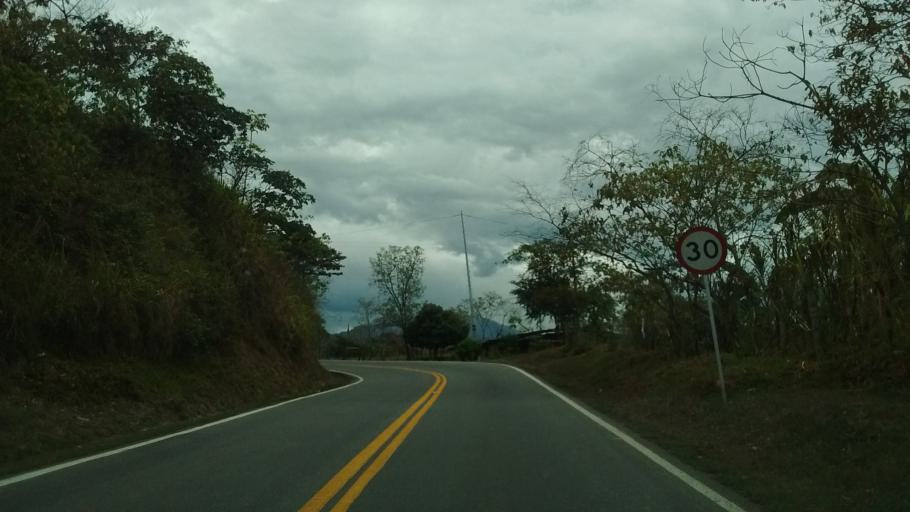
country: CO
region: Cauca
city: La Sierra
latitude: 2.2303
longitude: -76.7928
